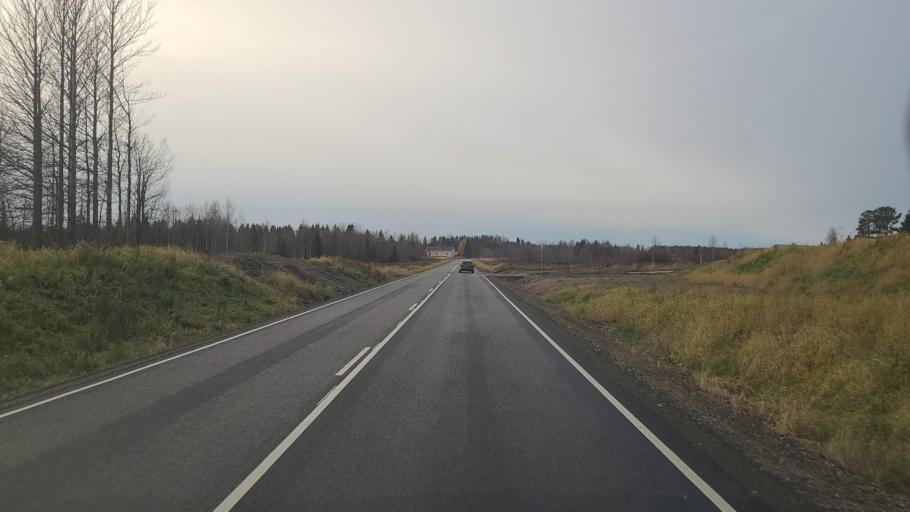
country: FI
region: Lapland
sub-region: Tunturi-Lappi
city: Kittilae
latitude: 67.8650
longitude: 24.9523
